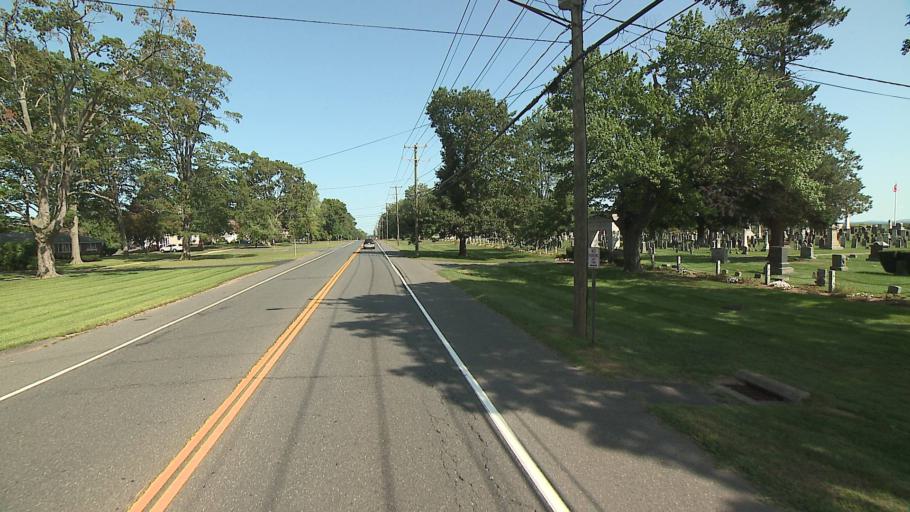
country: US
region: Connecticut
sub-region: Hartford County
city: Enfield
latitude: 41.9838
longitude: -72.5928
